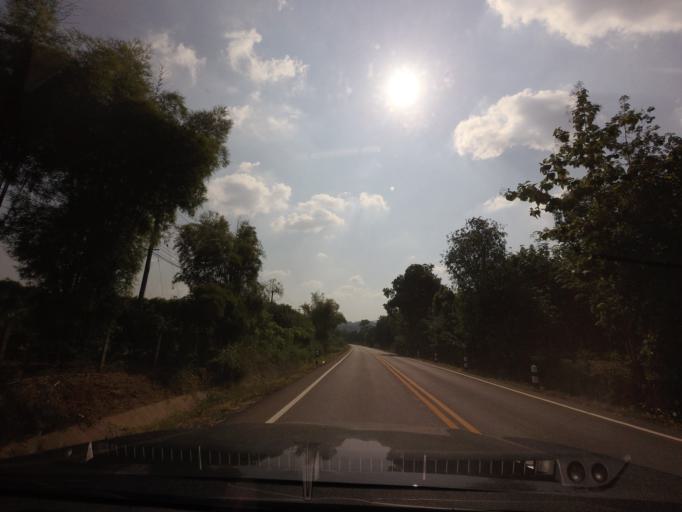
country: TH
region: Nan
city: Santi Suk
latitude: 18.9695
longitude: 100.9259
